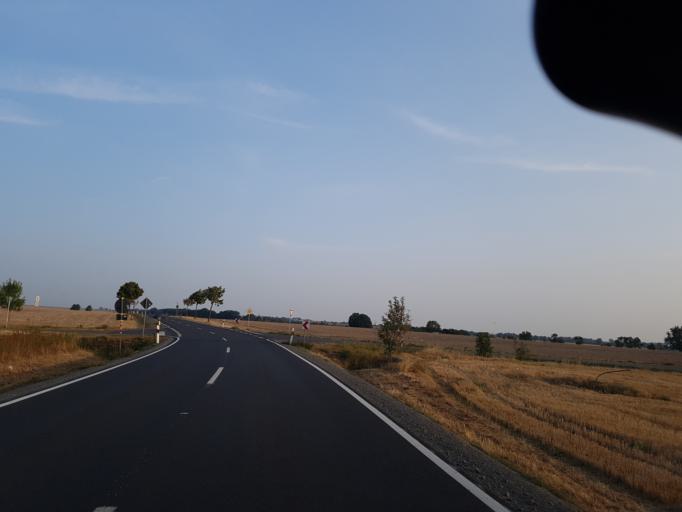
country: DE
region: Saxony
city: Zinna
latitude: 51.5774
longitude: 12.9649
